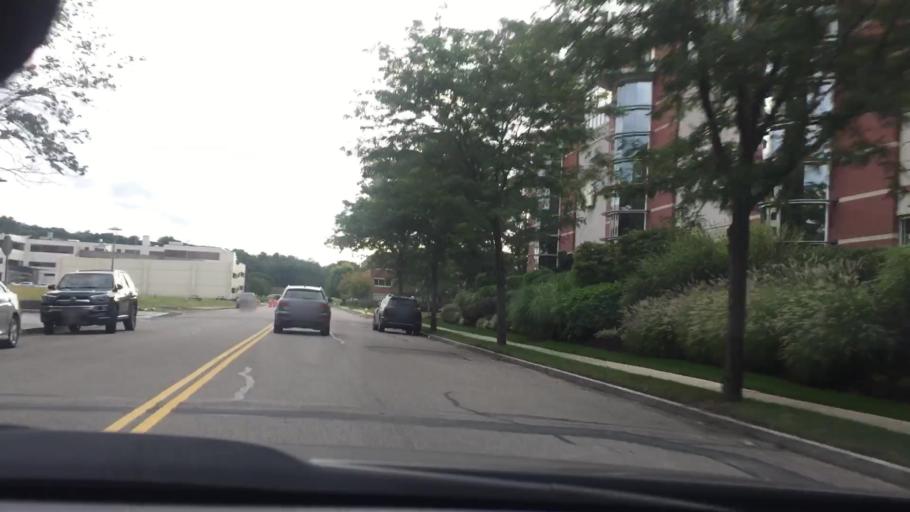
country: US
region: Massachusetts
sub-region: Norfolk County
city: Needham
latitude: 42.3009
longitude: -71.2185
